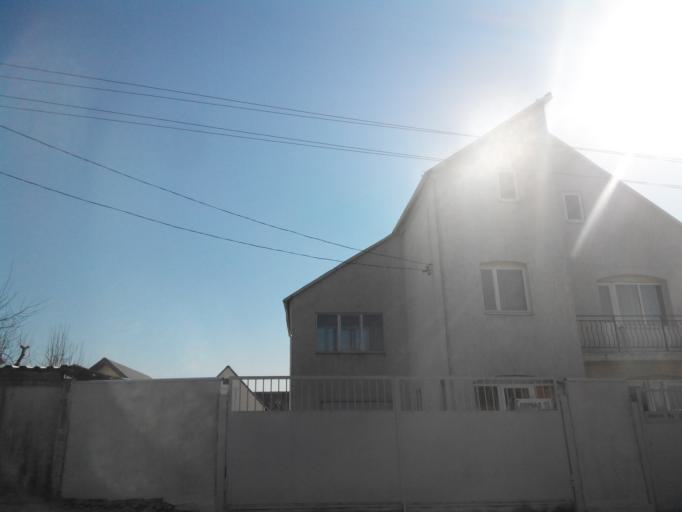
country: BY
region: Minsk
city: Zhdanovichy
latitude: 53.9239
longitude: 27.4011
